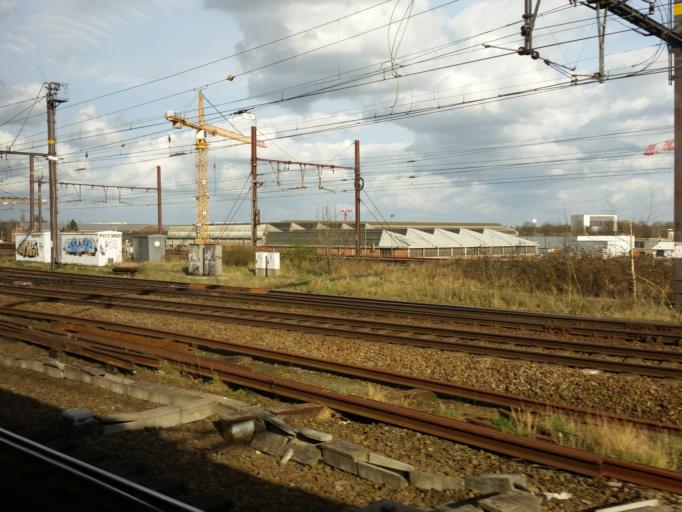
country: BE
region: Flanders
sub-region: Provincie Antwerpen
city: Mechelen
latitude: 51.0161
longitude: 4.4813
